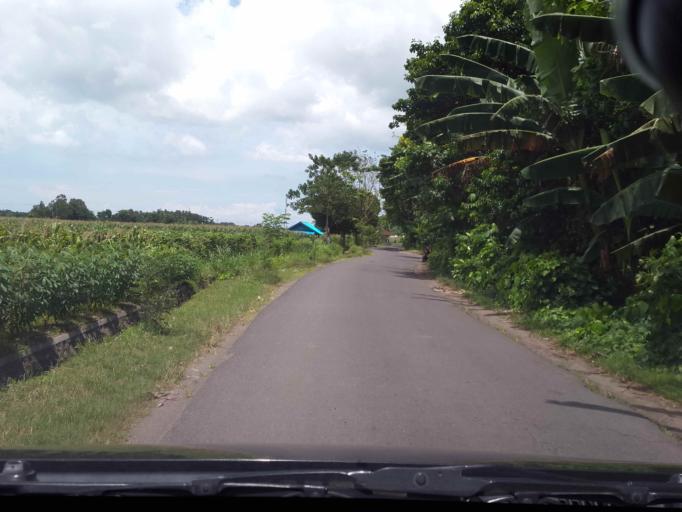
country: ID
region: West Nusa Tenggara
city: Jelateng Timur
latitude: -8.6923
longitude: 116.1045
